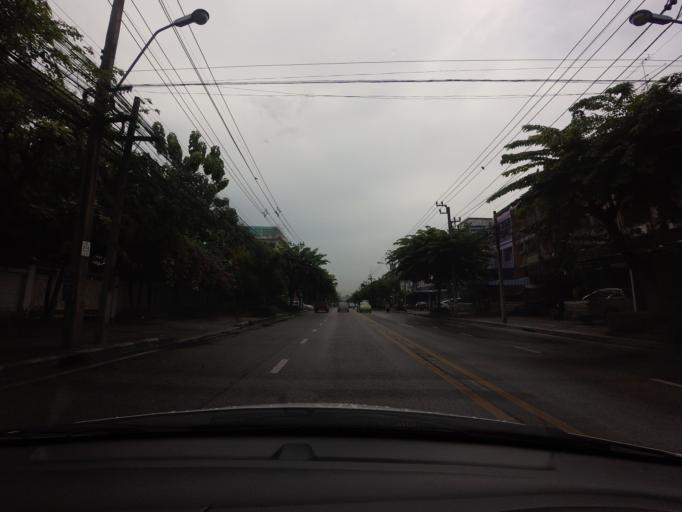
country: TH
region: Bangkok
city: Phra Khanong
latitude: 13.7100
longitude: 100.6280
